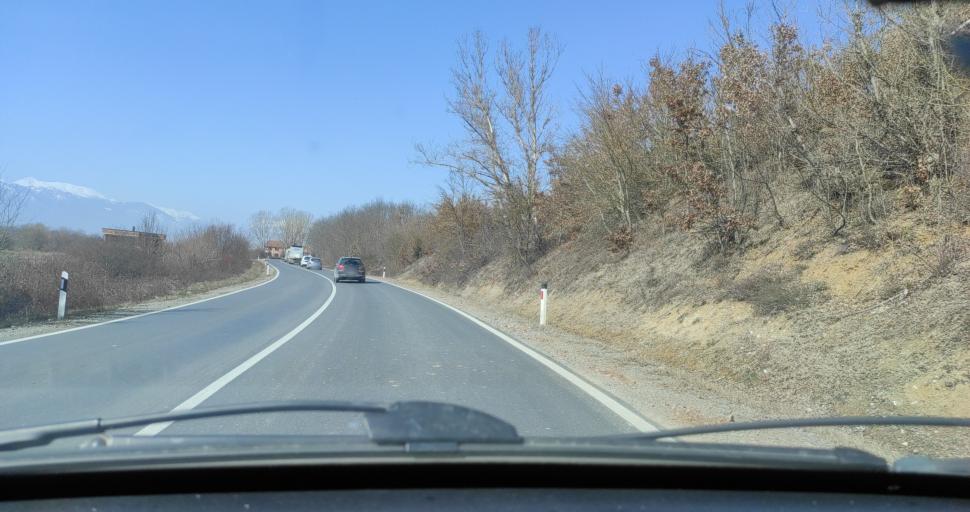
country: XK
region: Pec
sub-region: Komuna e Klines
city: Klina
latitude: 42.6000
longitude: 20.5280
